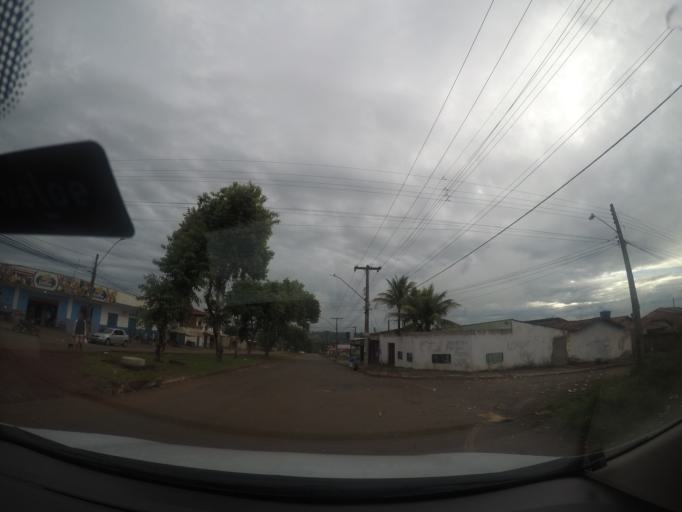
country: BR
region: Goias
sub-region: Goiania
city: Goiania
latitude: -16.5986
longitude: -49.3048
